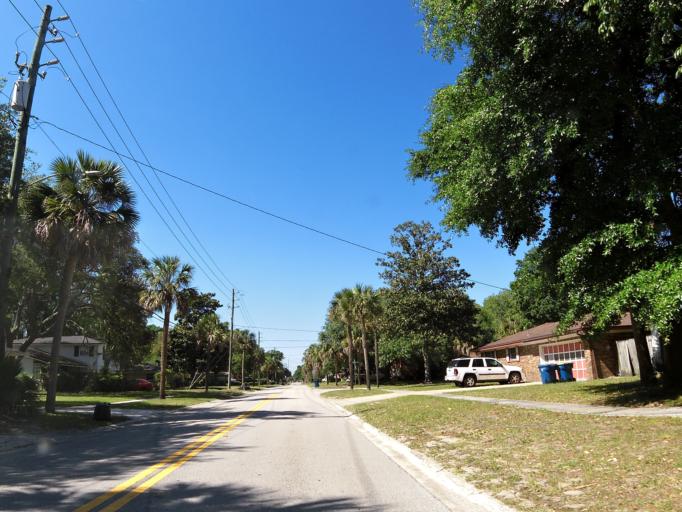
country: US
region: Florida
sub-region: Duval County
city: Jacksonville
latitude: 30.3407
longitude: -81.5685
